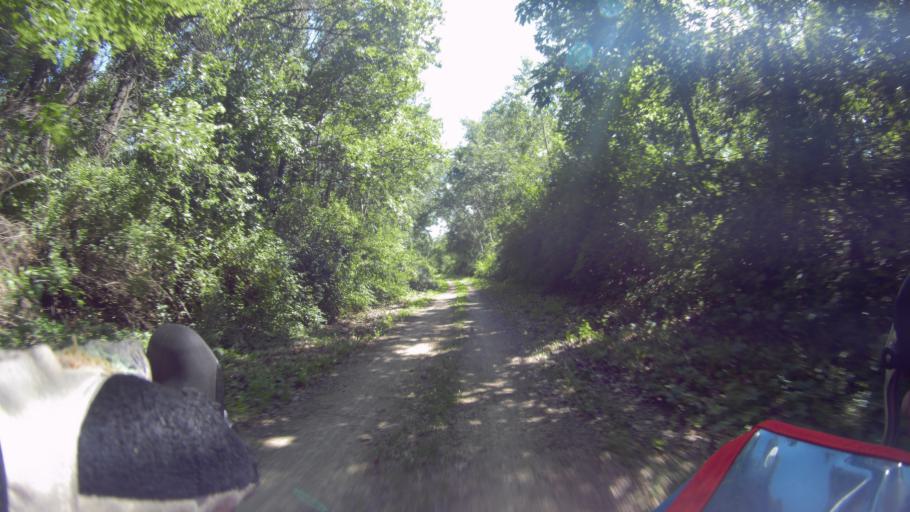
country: US
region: Wisconsin
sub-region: Dane County
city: Fitchburg
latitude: 42.9239
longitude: -89.5100
